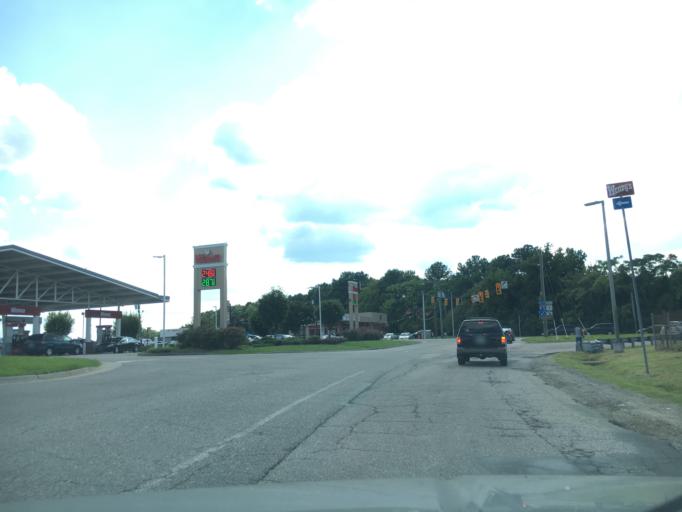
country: US
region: Virginia
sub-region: Henrico County
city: Lakeside
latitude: 37.6053
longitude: -77.4539
